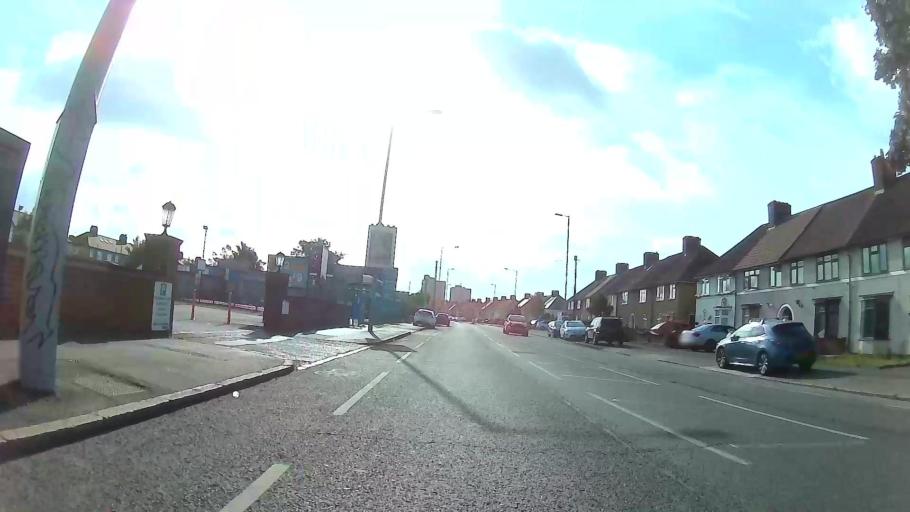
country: GB
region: England
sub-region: Greater London
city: Chadwell Heath
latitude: 51.5612
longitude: 0.1419
